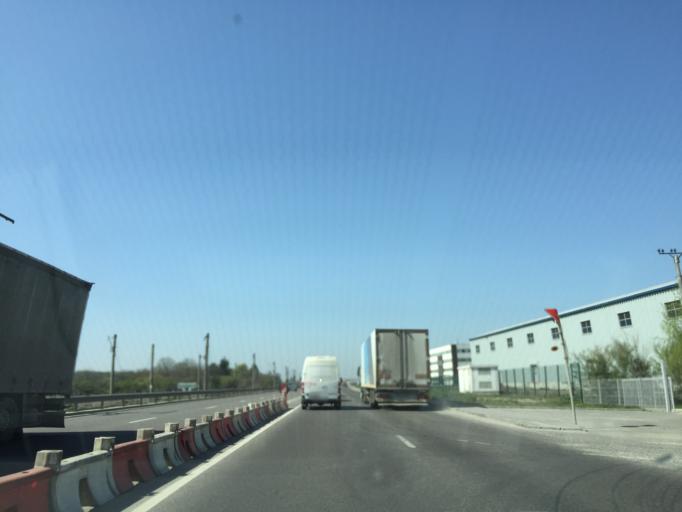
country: RO
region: Ilfov
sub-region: Comuna Otopeni
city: Otopeni
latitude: 44.5390
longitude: 26.0949
